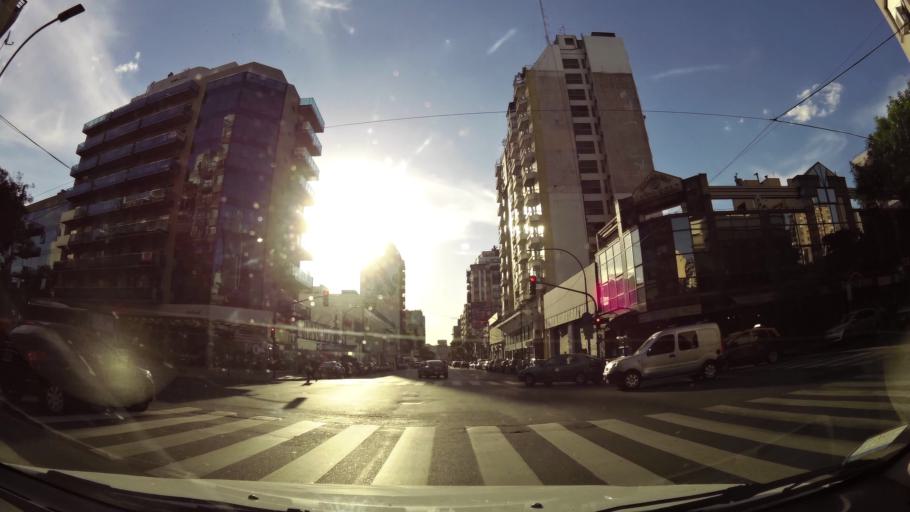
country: AR
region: Buenos Aires F.D.
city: Retiro
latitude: -34.5979
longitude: -58.4171
